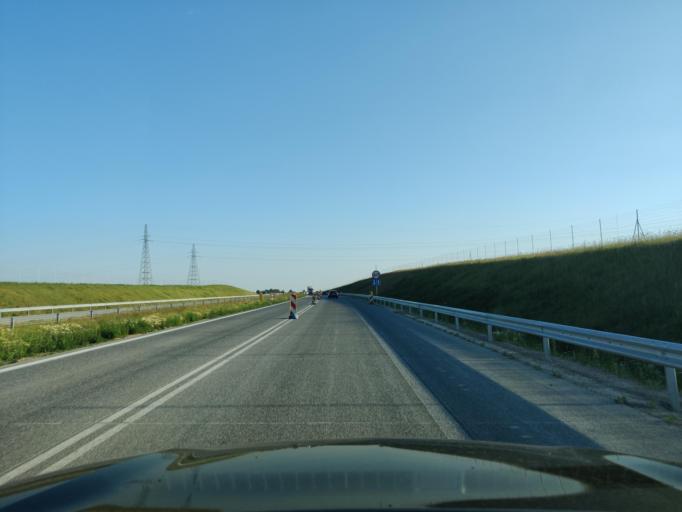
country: PL
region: Masovian Voivodeship
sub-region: Powiat mlawski
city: Mlawa
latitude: 53.1264
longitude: 20.4131
